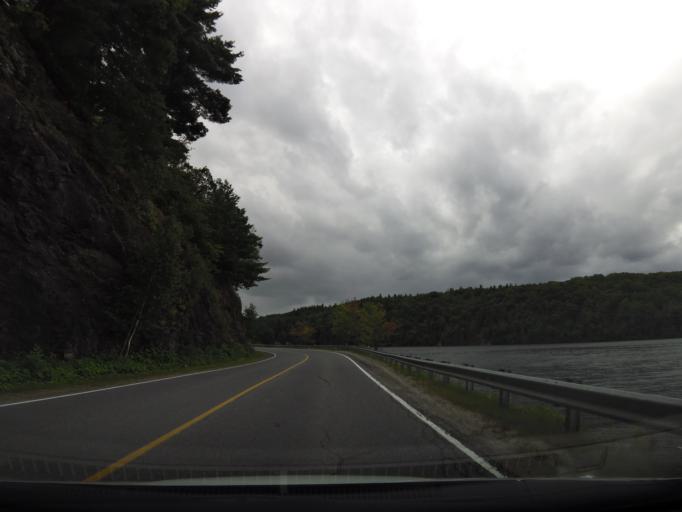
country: CA
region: Ontario
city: Perth
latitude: 44.6445
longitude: -76.5063
